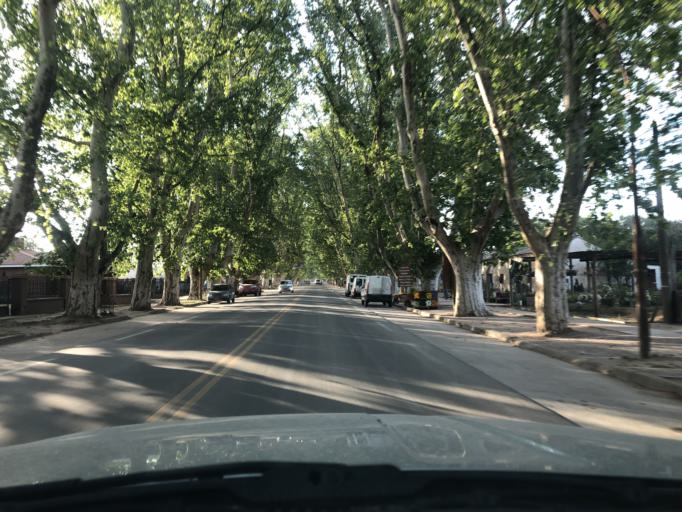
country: AR
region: Cordoba
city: Jesus Maria
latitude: -31.0129
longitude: -64.0715
